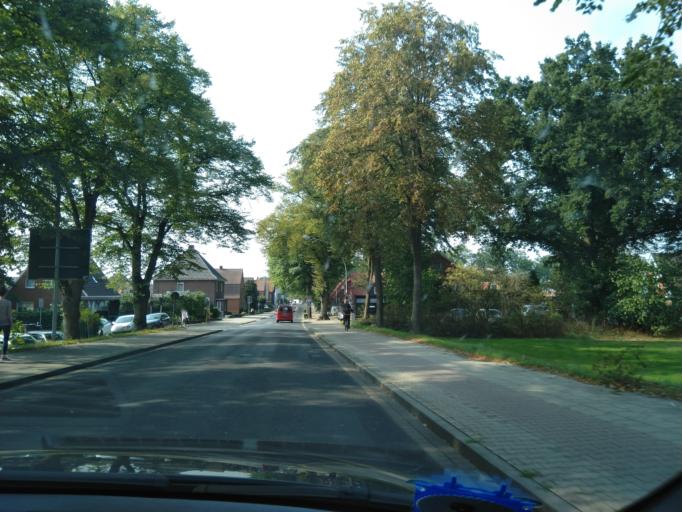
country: DE
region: Lower Saxony
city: Meppen
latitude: 52.6856
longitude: 7.2970
